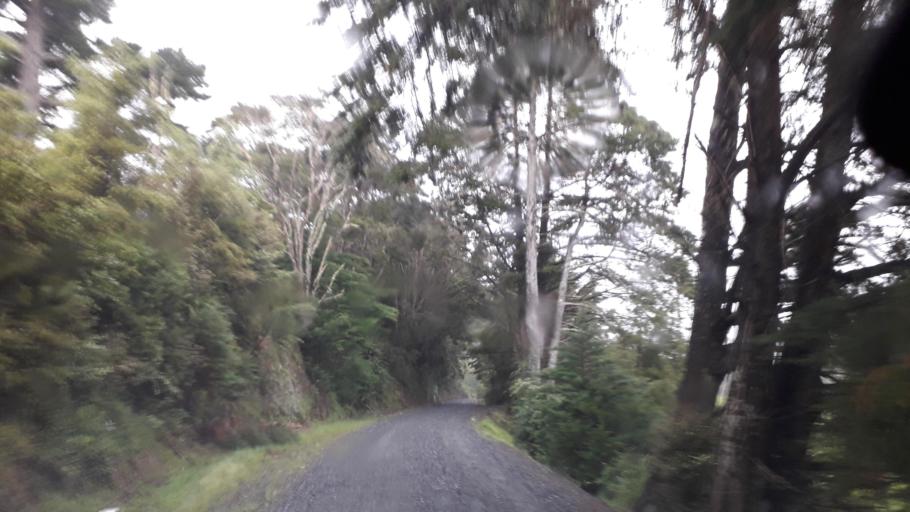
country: NZ
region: Northland
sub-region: Far North District
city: Waimate North
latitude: -35.1477
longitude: 173.7121
